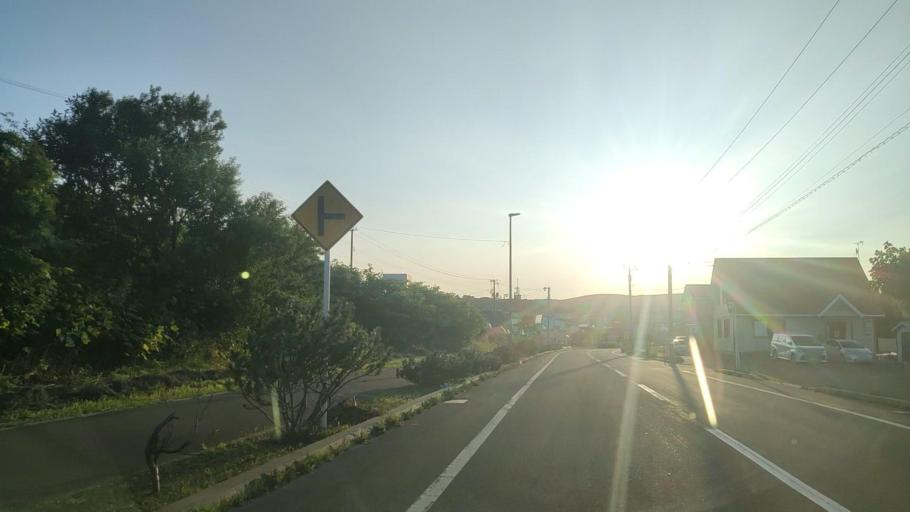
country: JP
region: Hokkaido
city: Wakkanai
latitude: 45.3924
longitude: 141.6981
